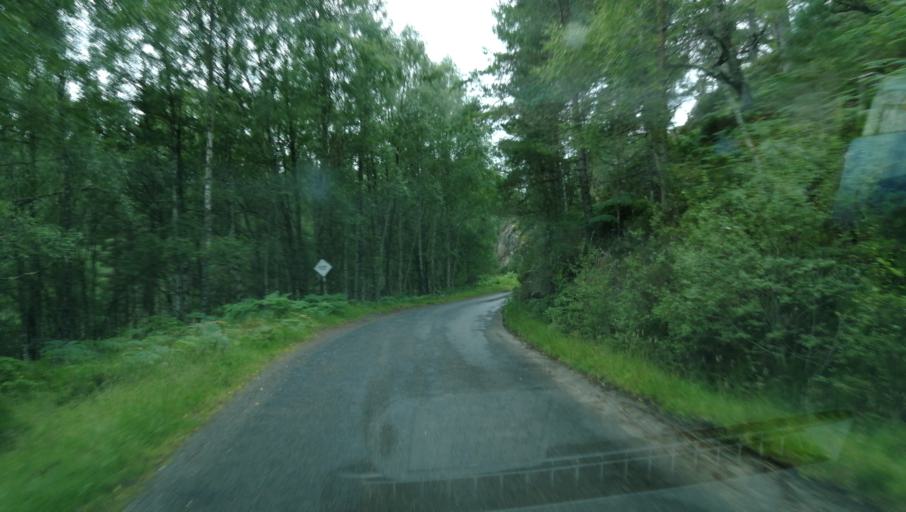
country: GB
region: Scotland
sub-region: Highland
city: Spean Bridge
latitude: 57.3085
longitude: -4.8664
